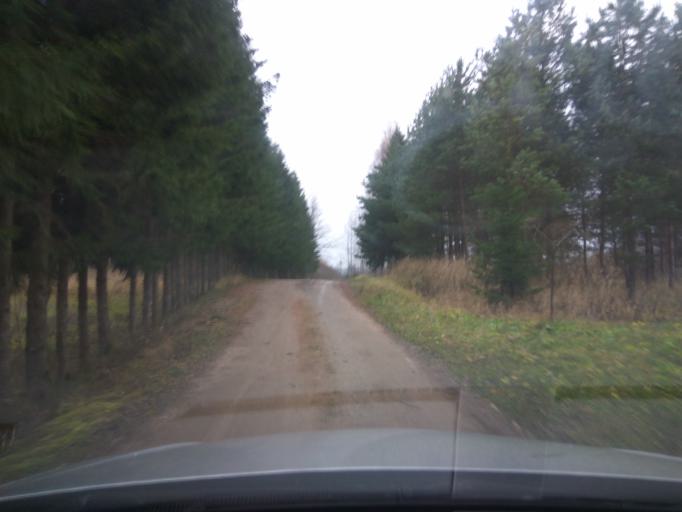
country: LV
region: Kuldigas Rajons
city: Kuldiga
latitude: 56.9320
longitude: 22.0094
